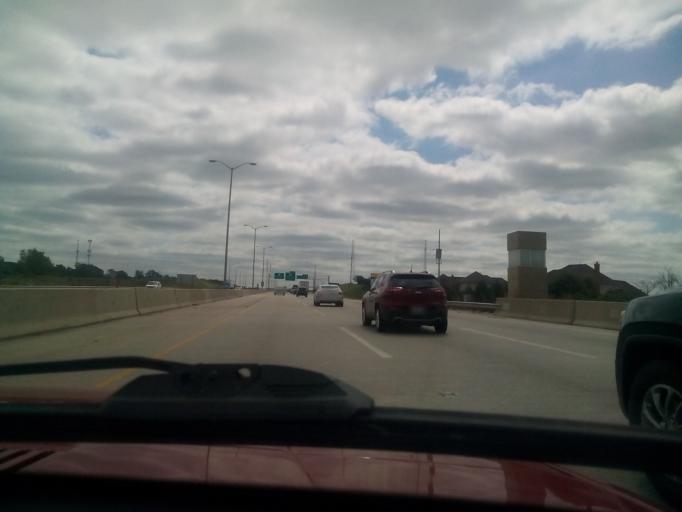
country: US
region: Illinois
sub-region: Cook County
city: Lemont
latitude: 41.6647
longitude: -88.0253
